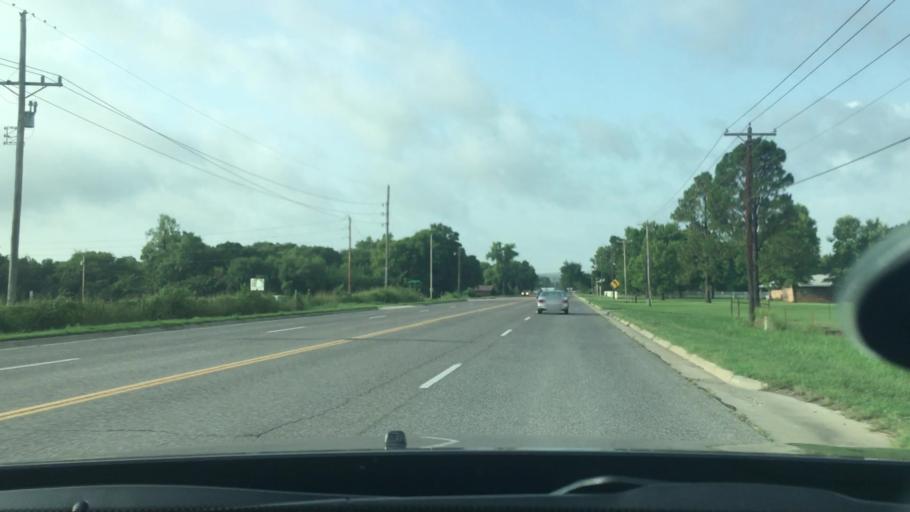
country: US
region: Oklahoma
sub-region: Murray County
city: Davis
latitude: 34.4787
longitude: -97.1313
